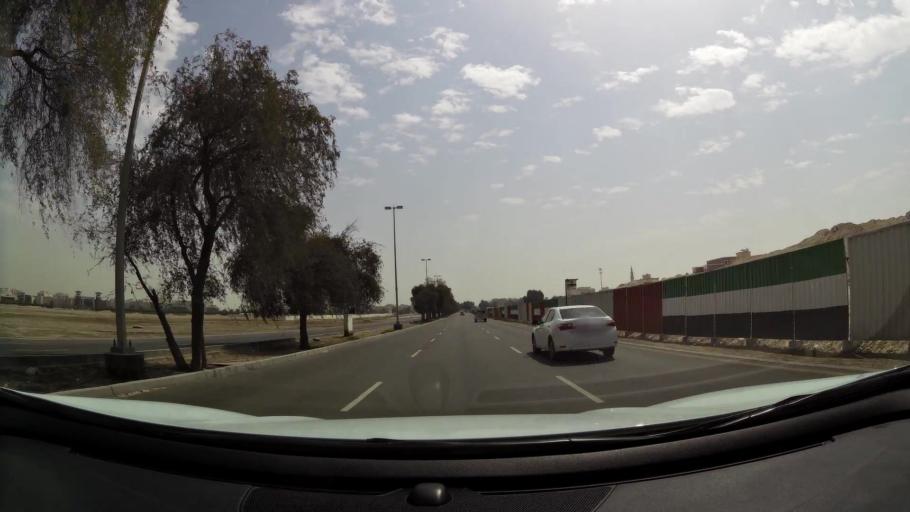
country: AE
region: Abu Dhabi
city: Abu Dhabi
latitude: 24.3111
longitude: 54.6133
